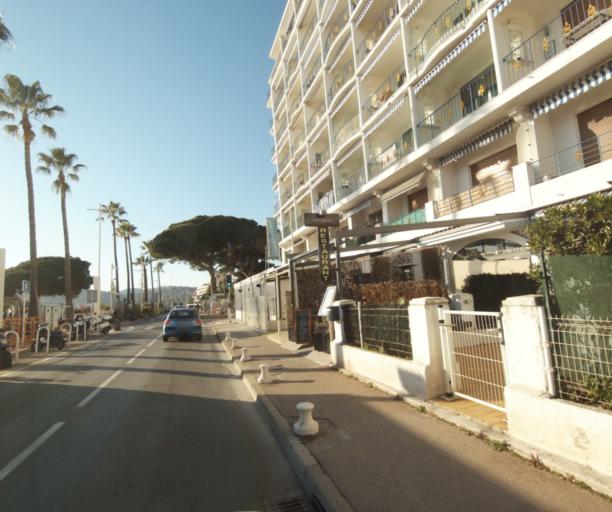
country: FR
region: Provence-Alpes-Cote d'Azur
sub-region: Departement des Alpes-Maritimes
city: Antibes
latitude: 43.5708
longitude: 7.1029
